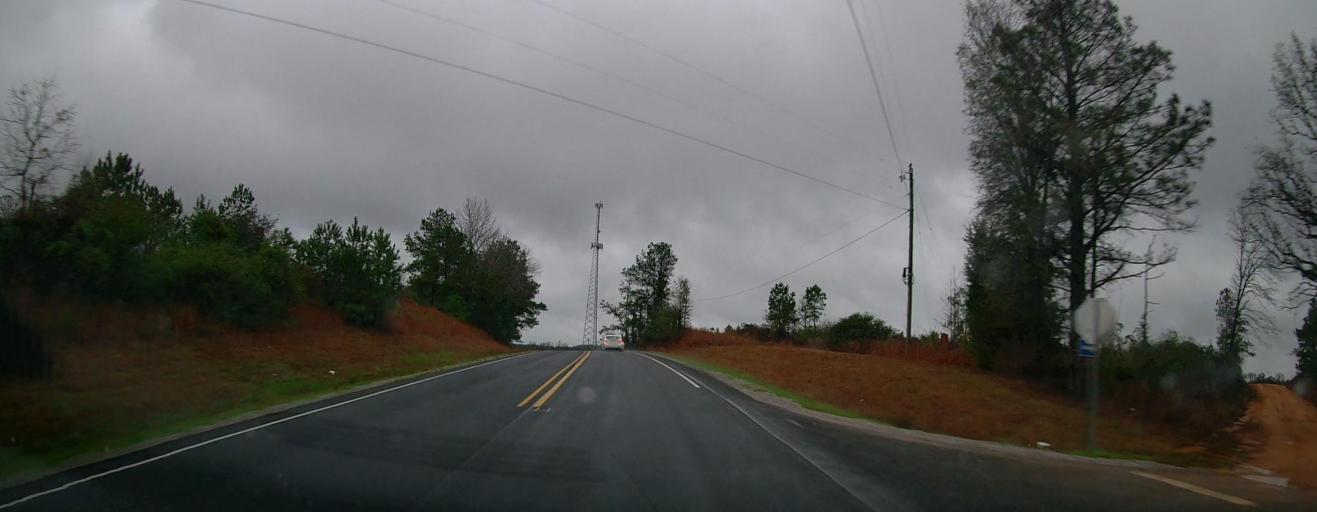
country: US
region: Alabama
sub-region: Chilton County
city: Clanton
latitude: 32.6396
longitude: -86.7524
